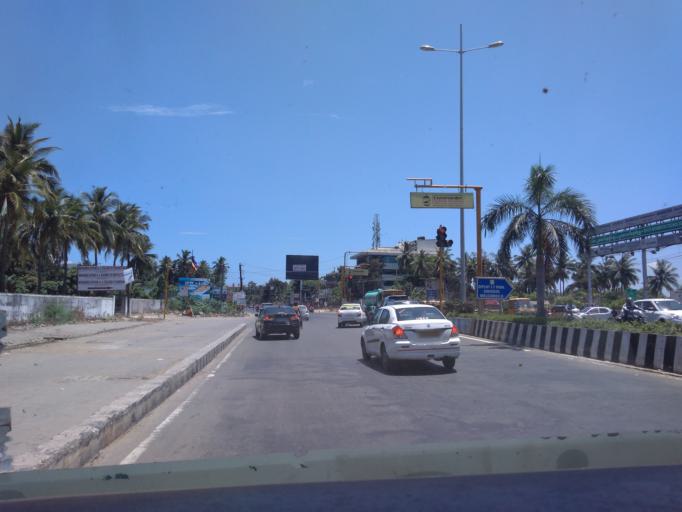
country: IN
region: Tamil Nadu
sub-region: Kancheepuram
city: Injambakkam
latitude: 12.8321
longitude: 80.2292
